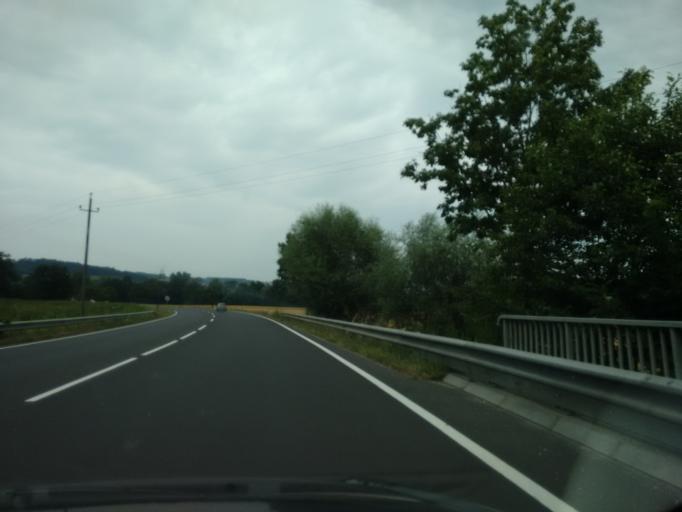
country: AT
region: Upper Austria
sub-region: Politischer Bezirk Grieskirchen
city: Bad Schallerbach
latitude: 48.1973
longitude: 13.9285
